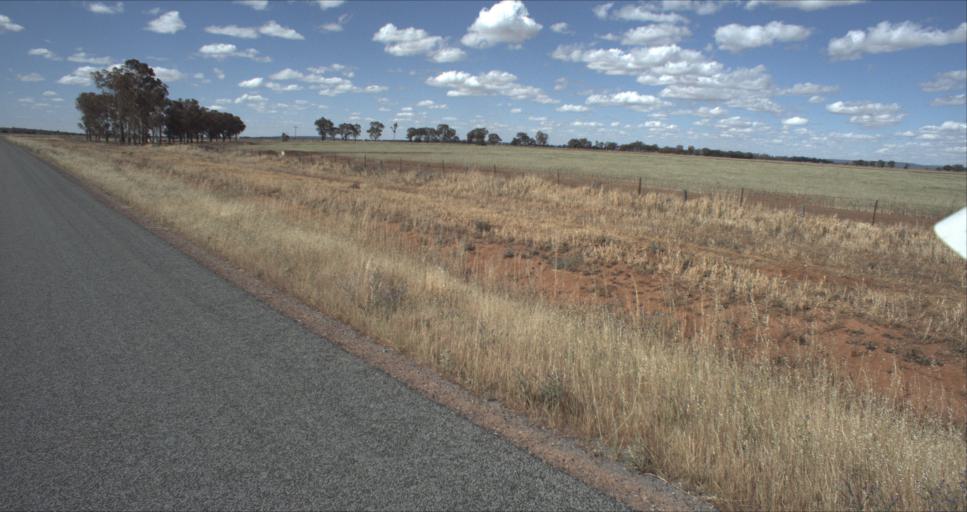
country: AU
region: New South Wales
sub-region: Leeton
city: Leeton
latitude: -34.4619
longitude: 146.2526
